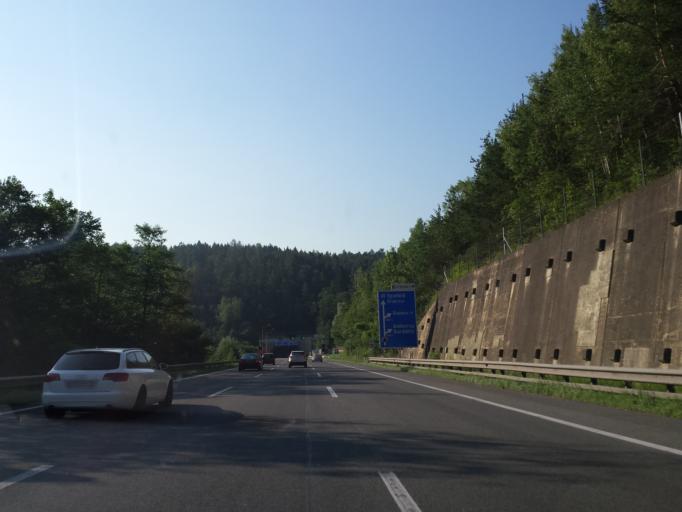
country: AT
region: Styria
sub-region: Politischer Bezirk Graz-Umgebung
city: Gratkorn
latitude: 47.1304
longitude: 15.3599
